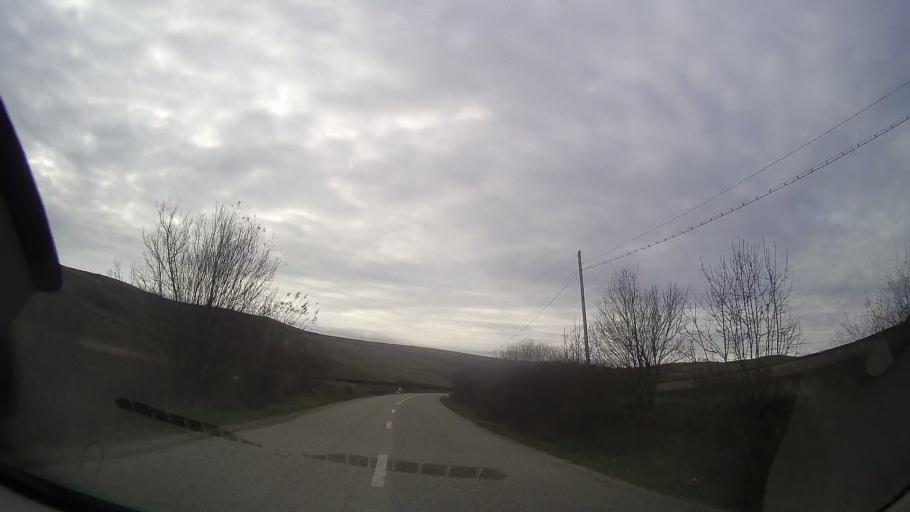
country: RO
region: Bistrita-Nasaud
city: Frunzi
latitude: 46.8945
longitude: 24.3060
